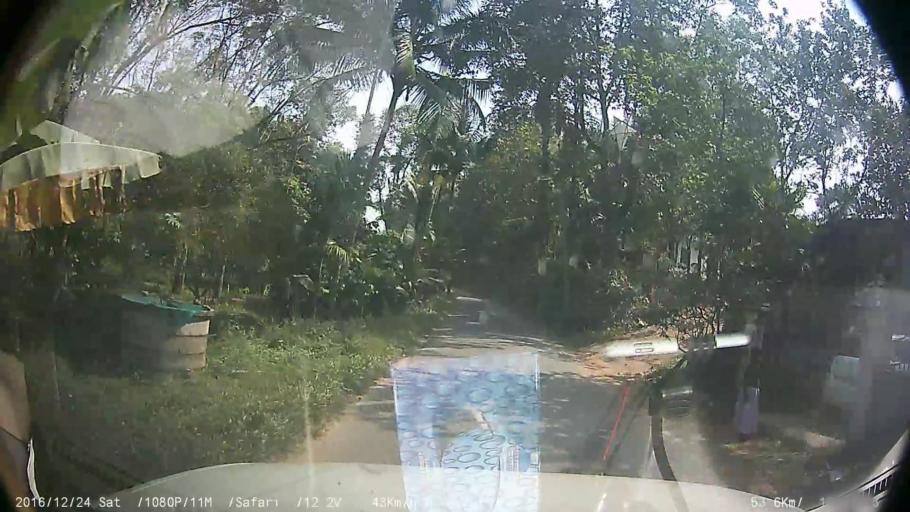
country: IN
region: Kerala
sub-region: Kottayam
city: Palackattumala
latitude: 9.8484
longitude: 76.7011
